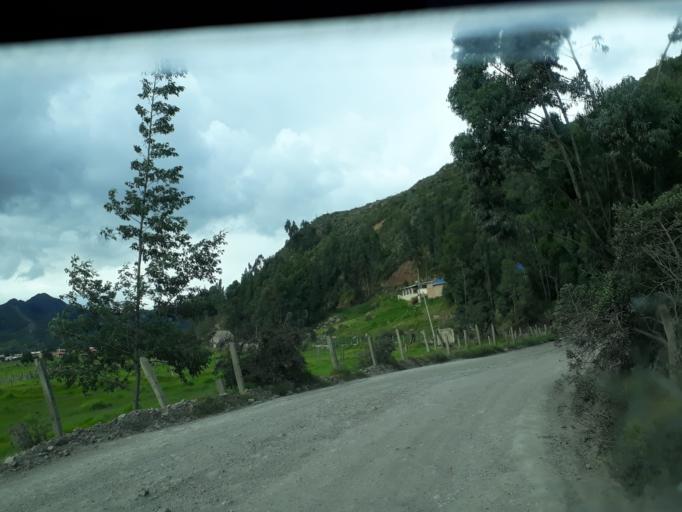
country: CO
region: Cundinamarca
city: Cucunuba
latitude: 5.2480
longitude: -73.7882
